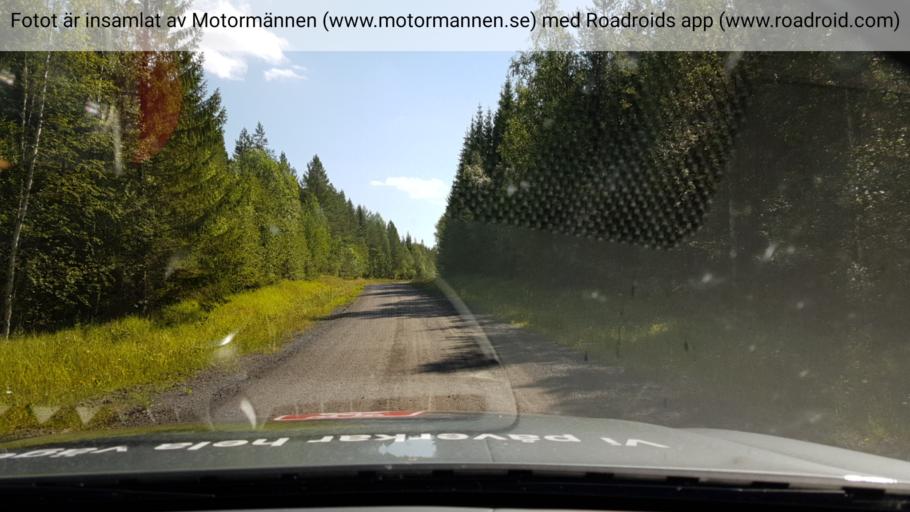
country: SE
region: Jaemtland
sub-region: Stroemsunds Kommun
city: Stroemsund
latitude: 63.3434
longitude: 15.3931
